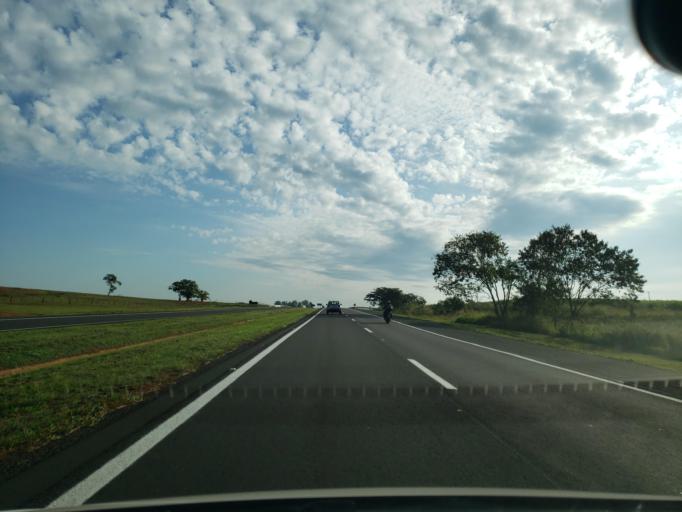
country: BR
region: Sao Paulo
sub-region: Guararapes
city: Guararapes
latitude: -21.2011
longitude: -50.5835
